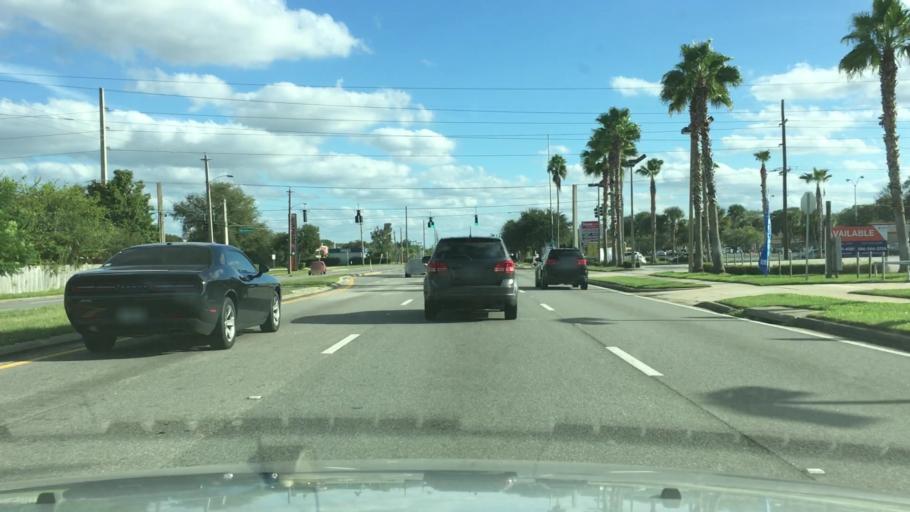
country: US
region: Florida
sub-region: Volusia County
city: Daytona Beach
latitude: 29.2077
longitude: -81.0422
